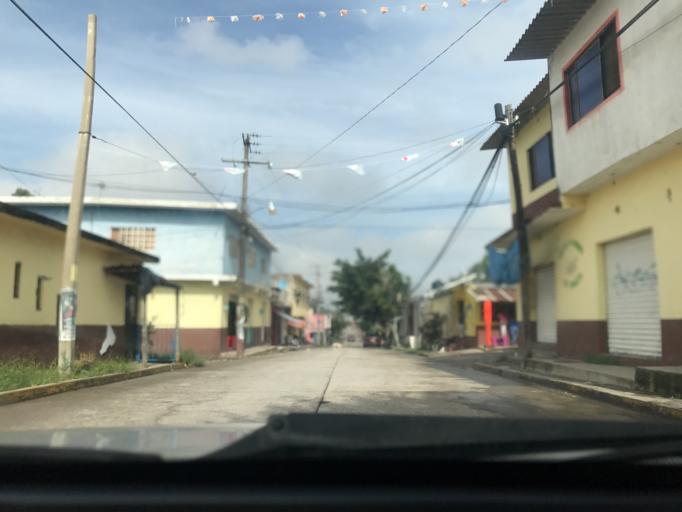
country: MX
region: Morelos
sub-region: Yecapixtla
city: Mixtlalcingo
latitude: 18.8030
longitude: -98.9106
